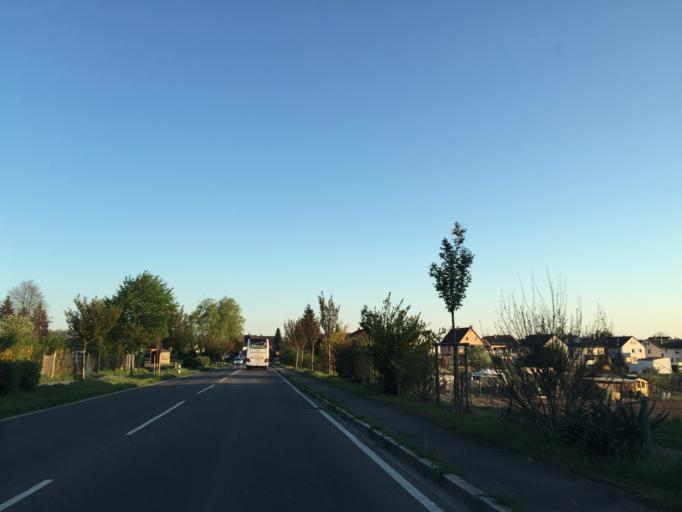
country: DE
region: Baden-Wuerttemberg
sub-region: Karlsruhe Region
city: Hemsbach
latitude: 49.5840
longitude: 8.6574
